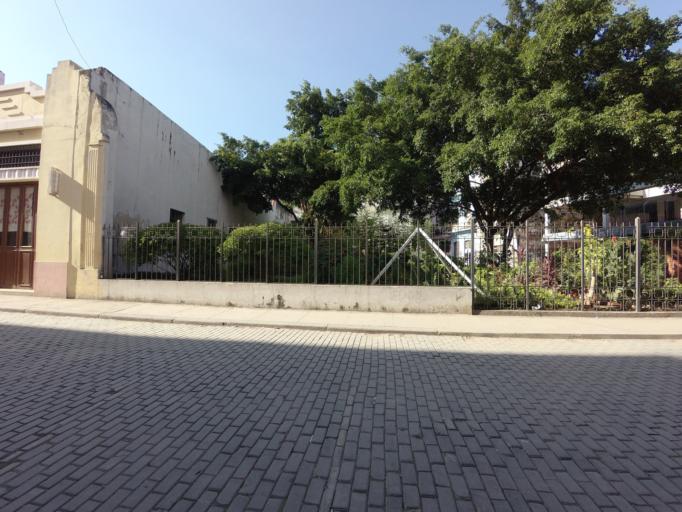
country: CU
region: La Habana
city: La Habana Vieja
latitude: 23.1361
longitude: -82.3529
